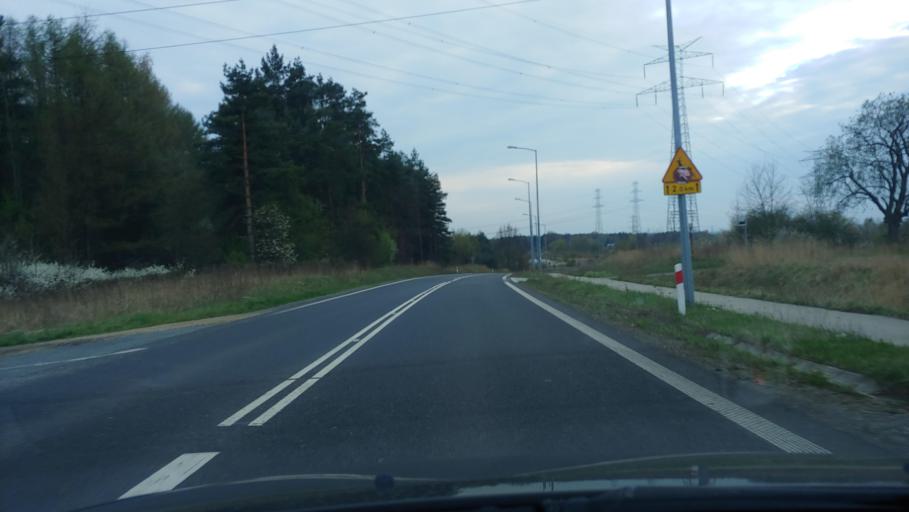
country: PL
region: Silesian Voivodeship
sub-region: Jaworzno
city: Jaworzno
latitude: 50.1663
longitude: 19.2842
